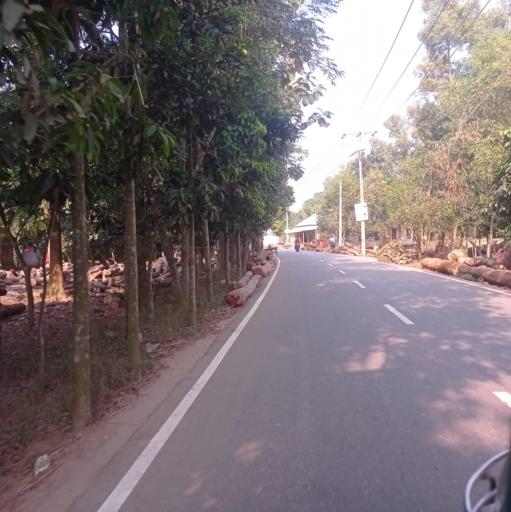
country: BD
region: Dhaka
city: Bhairab Bazar
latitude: 24.0613
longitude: 90.8404
